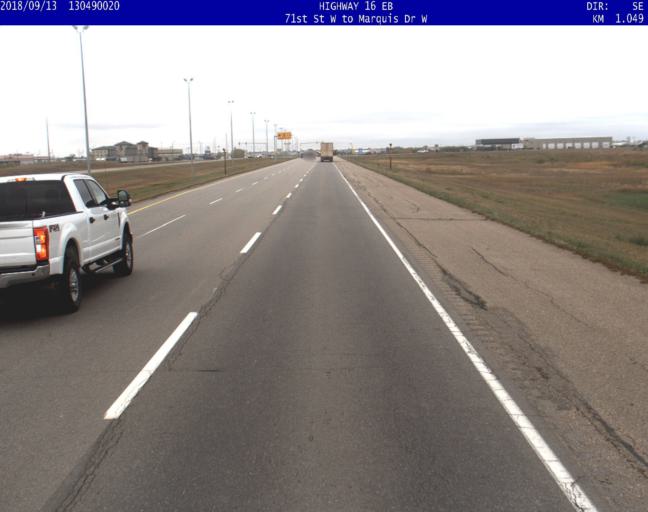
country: CA
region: Saskatchewan
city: Martensville
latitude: 52.1954
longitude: -106.6942
